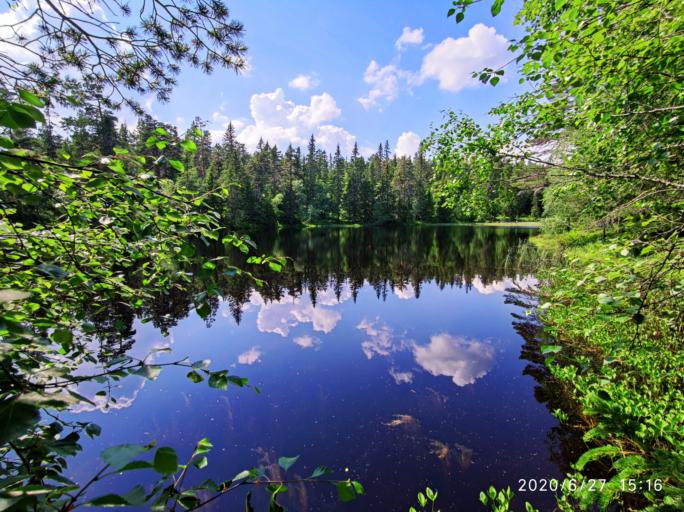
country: NO
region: Buskerud
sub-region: Kongsberg
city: Kongsberg
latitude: 59.6666
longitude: 9.5805
